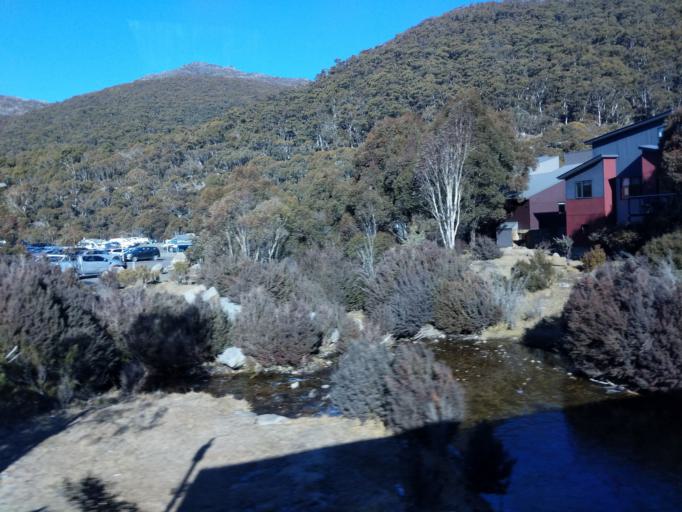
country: AU
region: New South Wales
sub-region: Snowy River
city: Jindabyne
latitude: -36.4998
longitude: 148.3112
